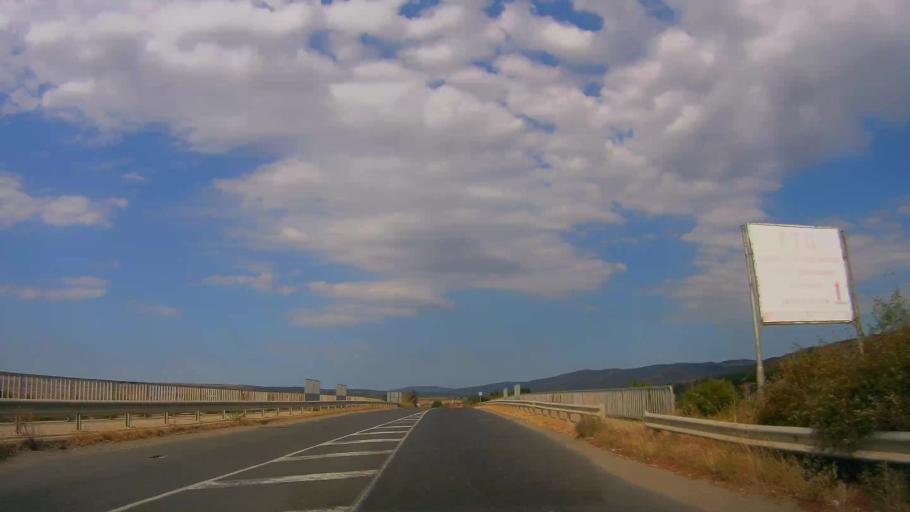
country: BG
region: Burgas
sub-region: Obshtina Aytos
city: Aytos
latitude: 42.7040
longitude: 27.2420
